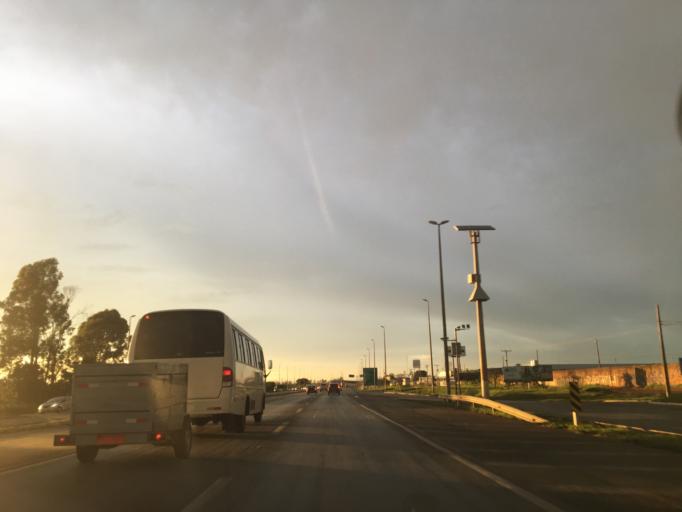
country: BR
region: Federal District
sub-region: Brasilia
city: Brasilia
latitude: -15.9938
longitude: -47.9861
